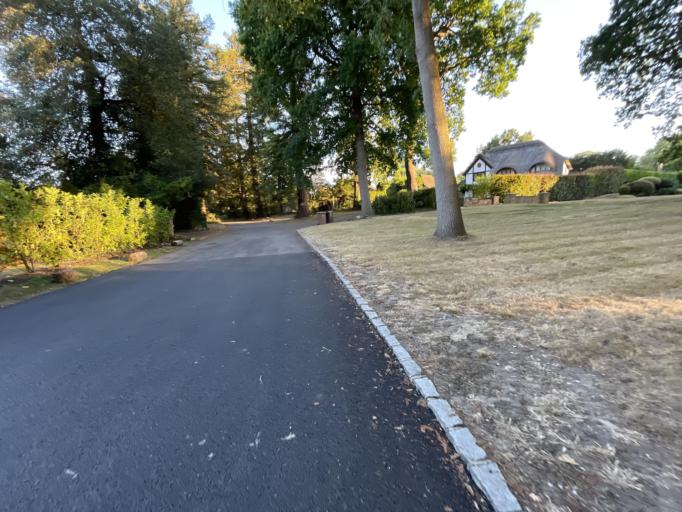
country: GB
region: England
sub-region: Surrey
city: East Horsley
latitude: 51.2696
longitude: -0.4280
